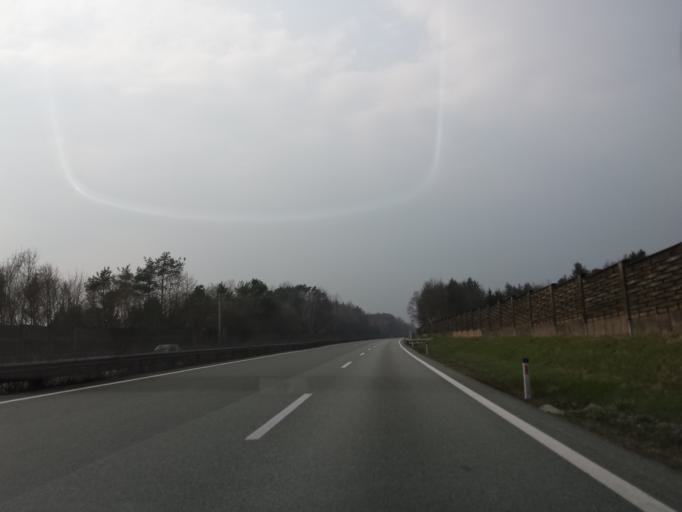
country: AT
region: Styria
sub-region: Politischer Bezirk Weiz
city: Sinabelkirchen
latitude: 47.1008
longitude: 15.7893
